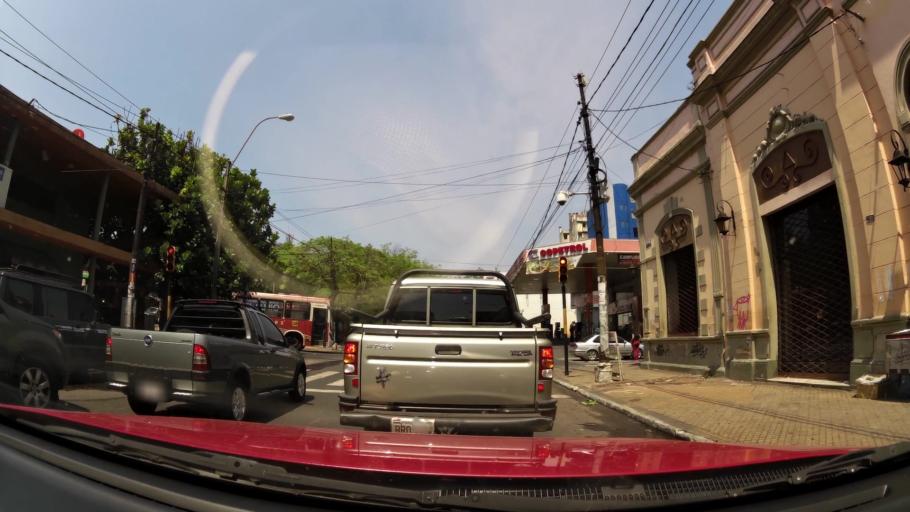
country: PY
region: Asuncion
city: Asuncion
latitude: -25.2801
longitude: -57.6426
